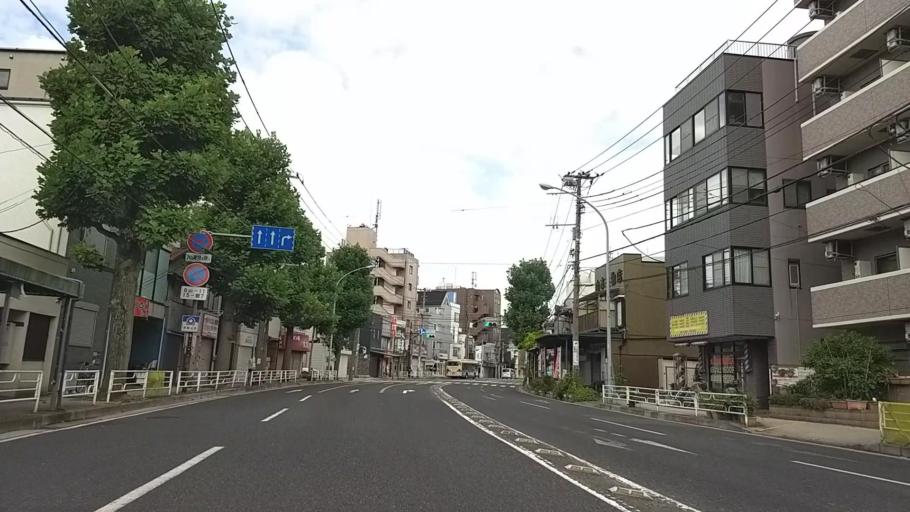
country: JP
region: Kanagawa
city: Yokohama
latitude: 35.4323
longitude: 139.6509
